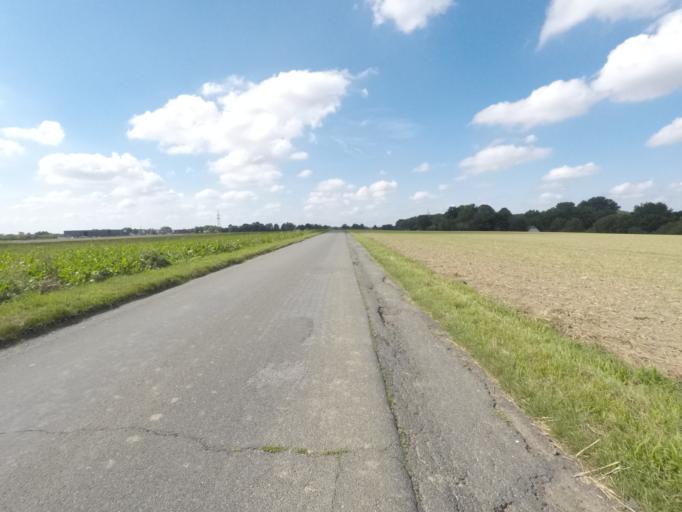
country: DE
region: North Rhine-Westphalia
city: Enger
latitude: 52.1162
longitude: 8.5667
